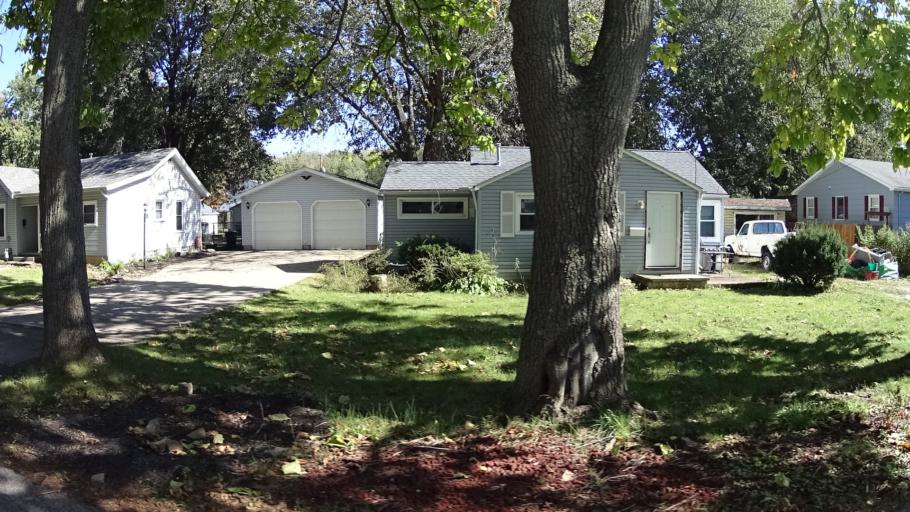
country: US
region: Ohio
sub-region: Lorain County
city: Amherst
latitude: 41.3948
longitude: -82.2141
